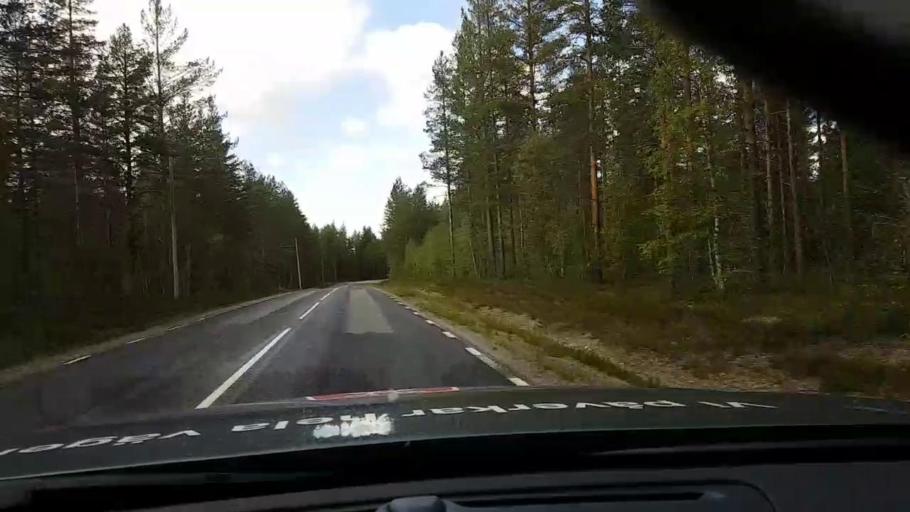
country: SE
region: Vaesterbotten
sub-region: Asele Kommun
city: Asele
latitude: 63.7922
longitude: 17.5809
